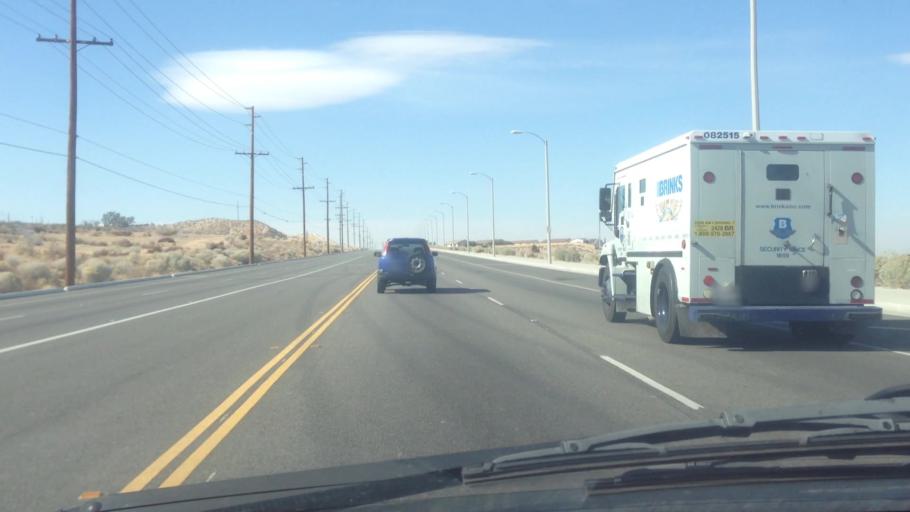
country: US
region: California
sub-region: Los Angeles County
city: Desert View Highlands
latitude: 34.5726
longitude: -118.1407
